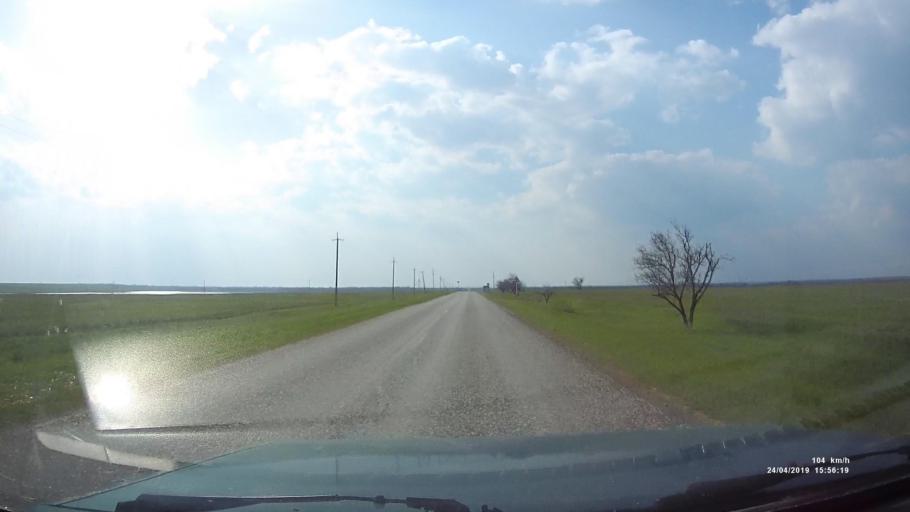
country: RU
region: Kalmykiya
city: Yashalta
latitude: 46.5969
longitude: 42.5313
